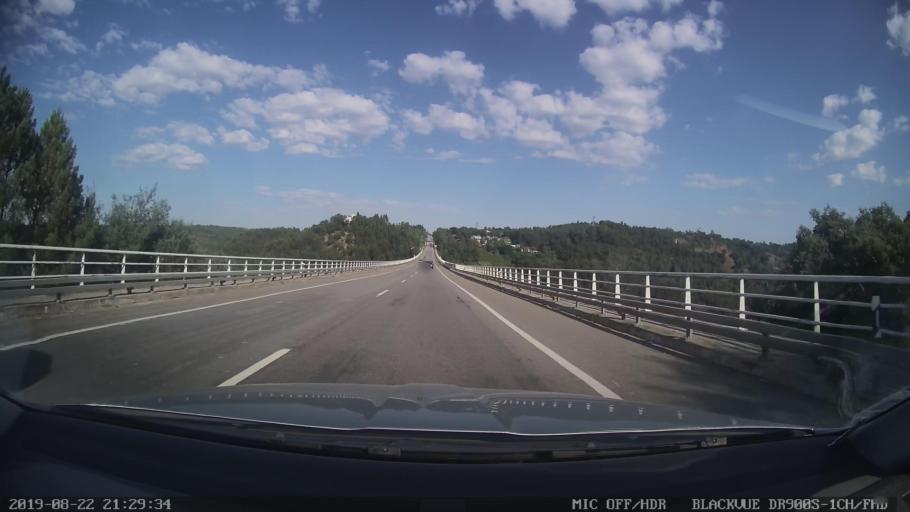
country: PT
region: Leiria
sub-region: Pedrogao Grande
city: Pedrogao Grande
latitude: 39.9033
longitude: -8.1373
